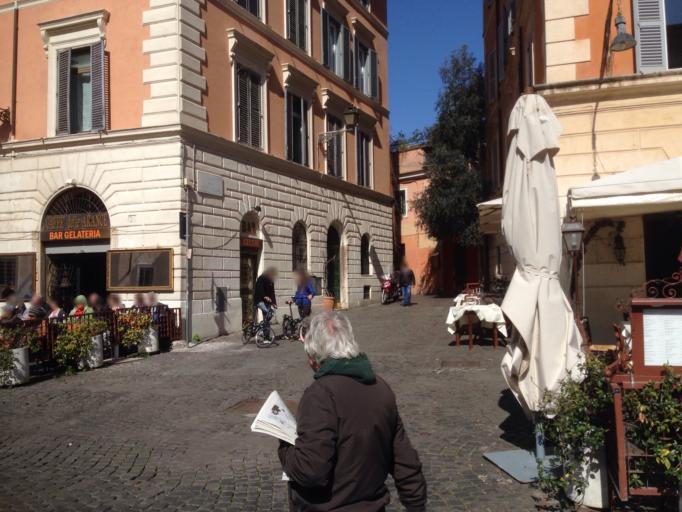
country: VA
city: Vatican City
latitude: 41.8897
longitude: 12.4703
